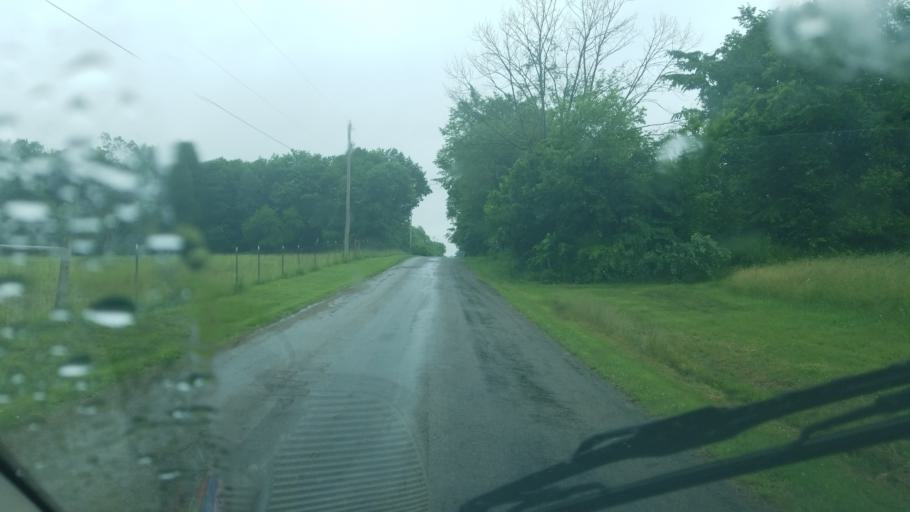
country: US
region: Ohio
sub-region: Sandusky County
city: Bellville
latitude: 40.6237
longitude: -82.4367
